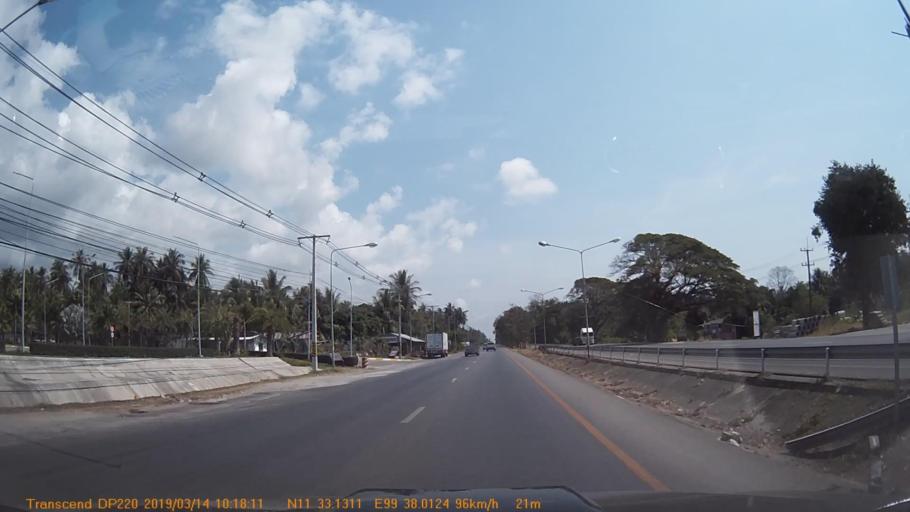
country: TH
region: Prachuap Khiri Khan
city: Thap Sakae
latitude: 11.5478
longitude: 99.6311
